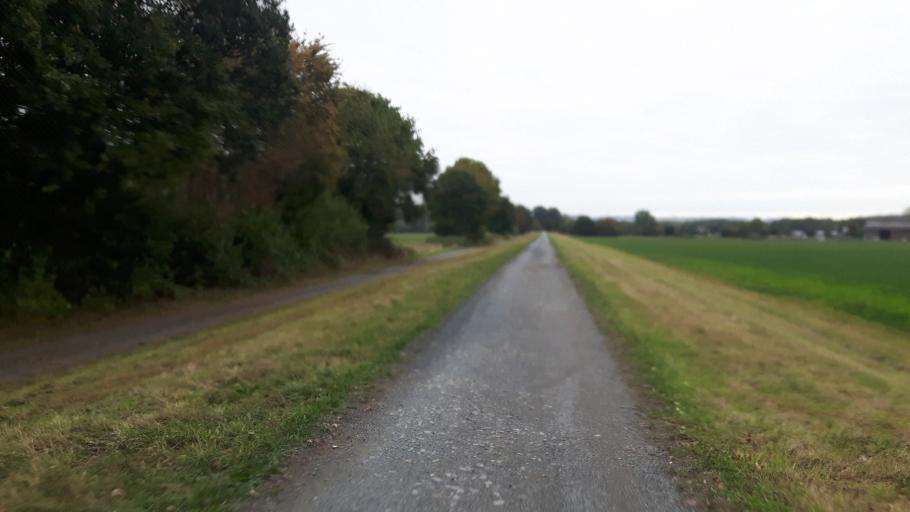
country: DE
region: North Rhine-Westphalia
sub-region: Regierungsbezirk Koln
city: Hennef
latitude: 50.7909
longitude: 7.2735
